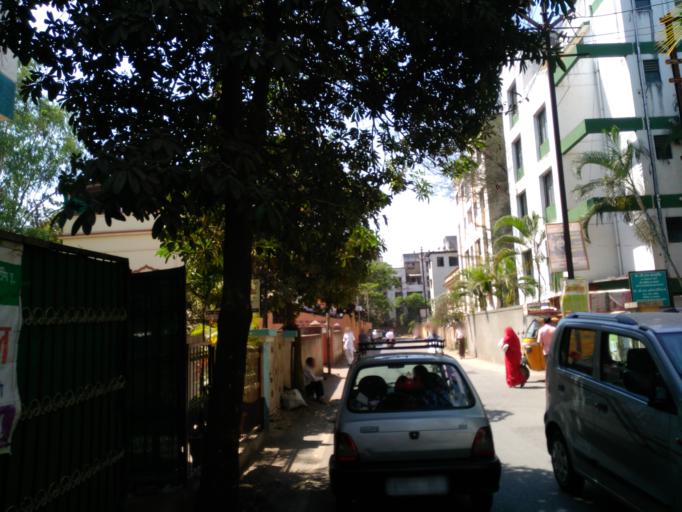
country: IN
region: Maharashtra
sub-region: Pune Division
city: Pune
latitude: 18.4538
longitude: 73.8533
